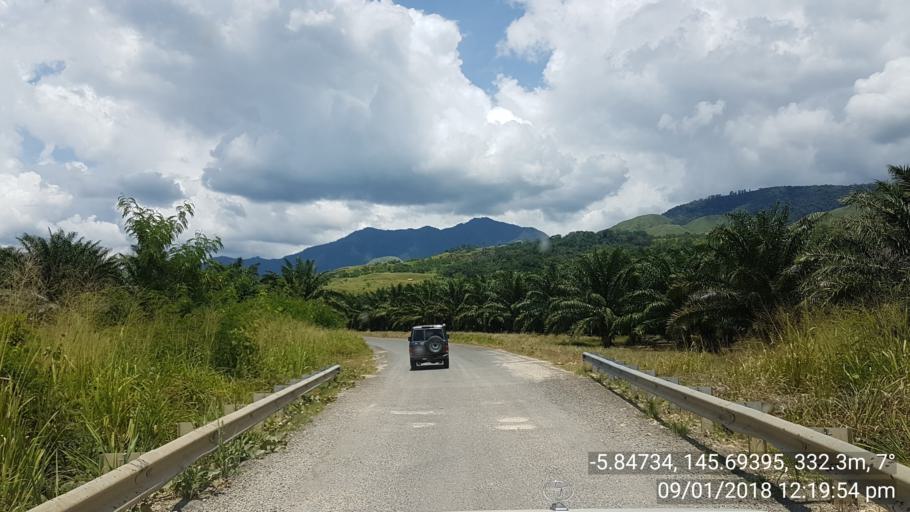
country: PG
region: Eastern Highlands
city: Goroka
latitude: -5.8472
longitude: 145.6938
